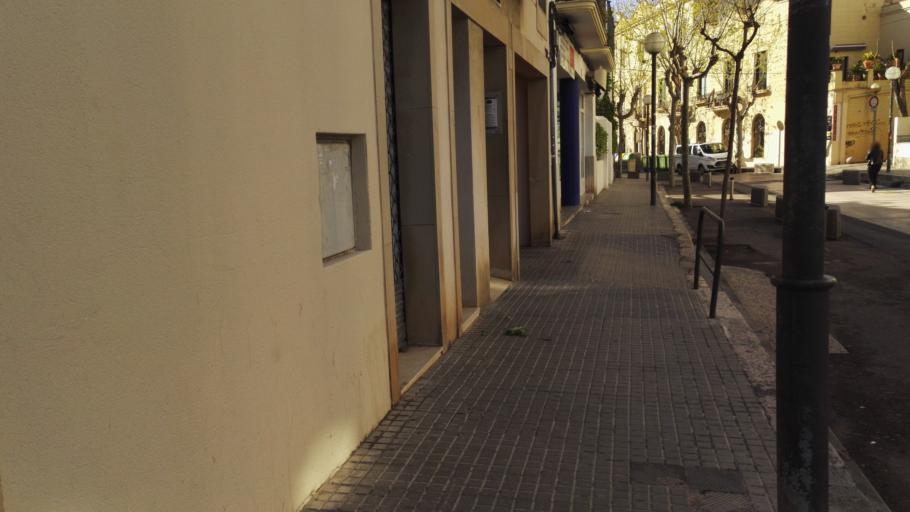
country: ES
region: Catalonia
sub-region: Provincia de Barcelona
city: Sitges
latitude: 41.2364
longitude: 1.8056
